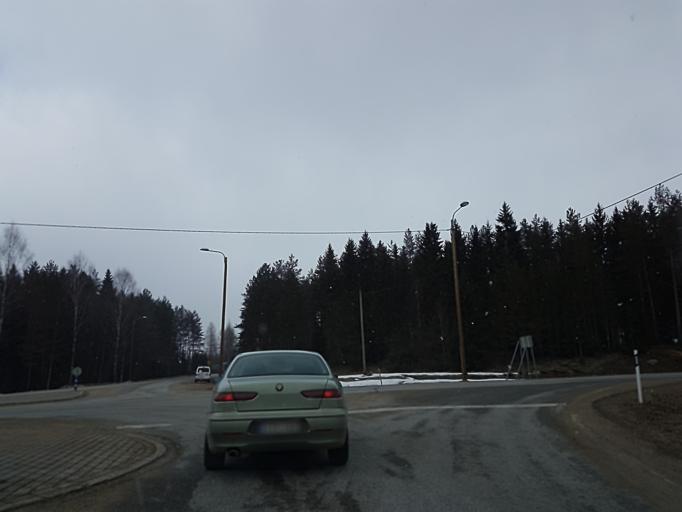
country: FI
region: North Karelia
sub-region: Joensuu
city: Outokumpu
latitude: 62.7352
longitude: 29.0525
